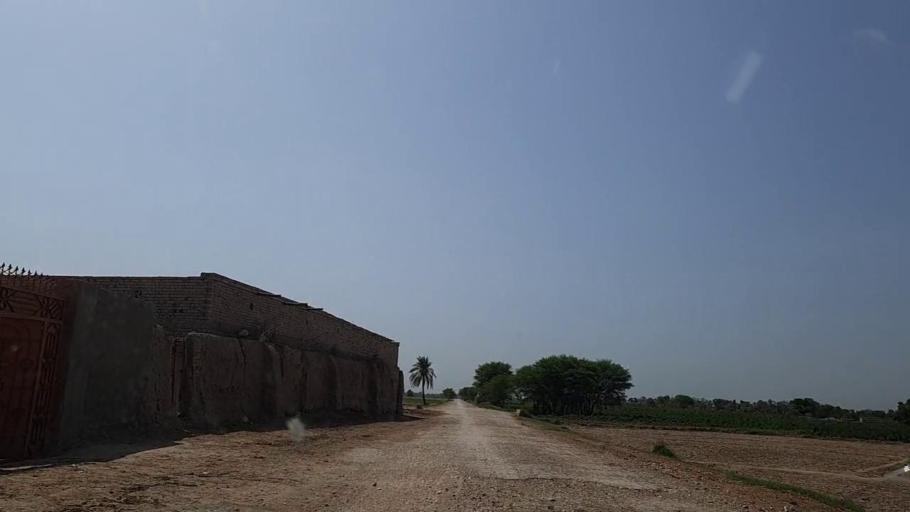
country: PK
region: Sindh
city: Naushahro Firoz
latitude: 26.8496
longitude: 68.0107
